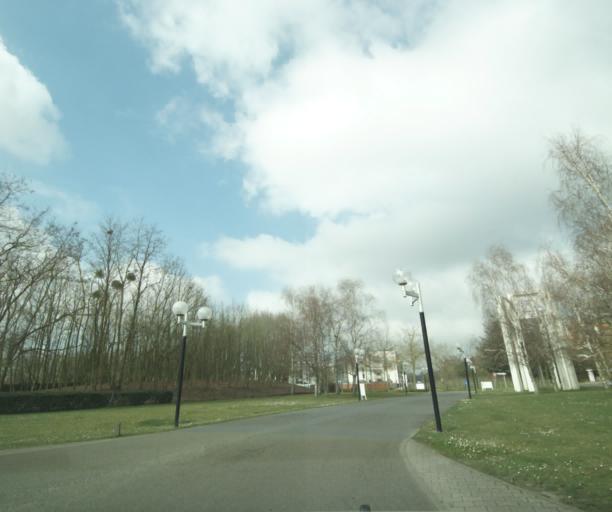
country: FR
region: Ile-de-France
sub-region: Departement du Val-d'Oise
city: Vaureal
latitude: 49.0425
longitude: 2.0300
